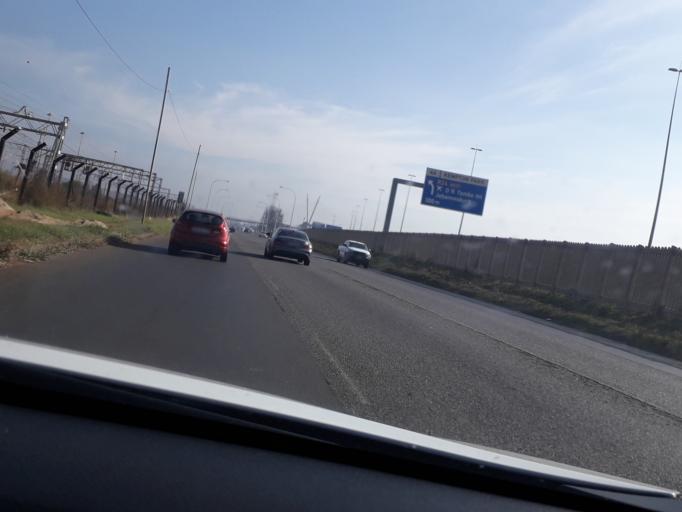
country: ZA
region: Gauteng
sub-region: City of Johannesburg Metropolitan Municipality
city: Modderfontein
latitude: -26.1413
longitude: 28.2201
